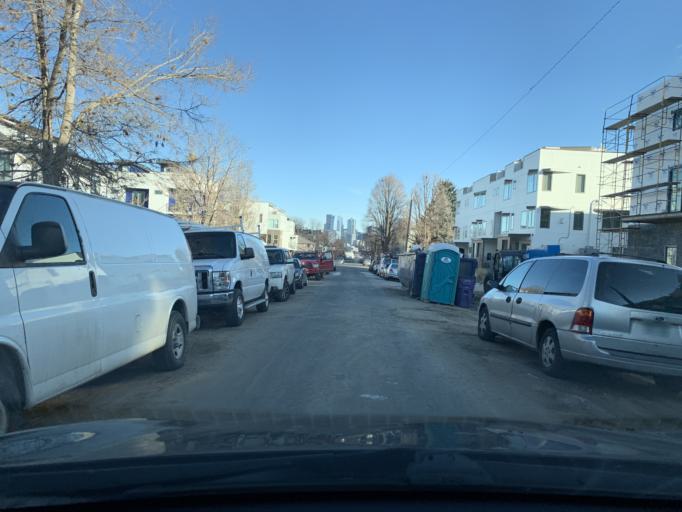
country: US
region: Colorado
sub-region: Jefferson County
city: Edgewater
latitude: 39.7464
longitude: -105.0295
